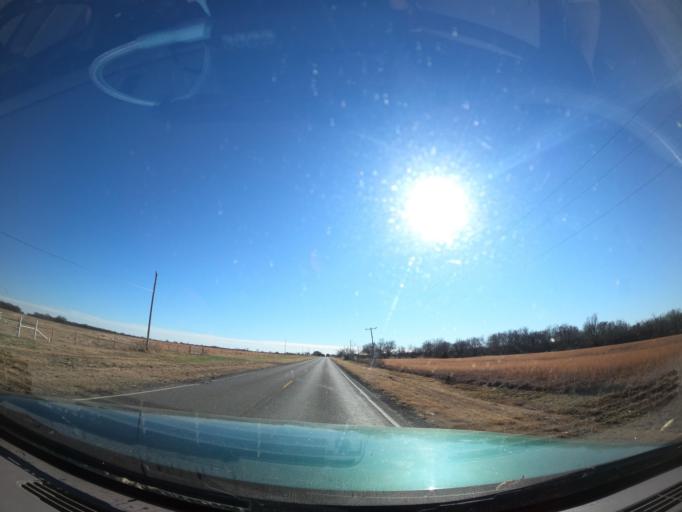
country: US
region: Oklahoma
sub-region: Muskogee County
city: Haskell
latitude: 35.6740
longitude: -95.6422
